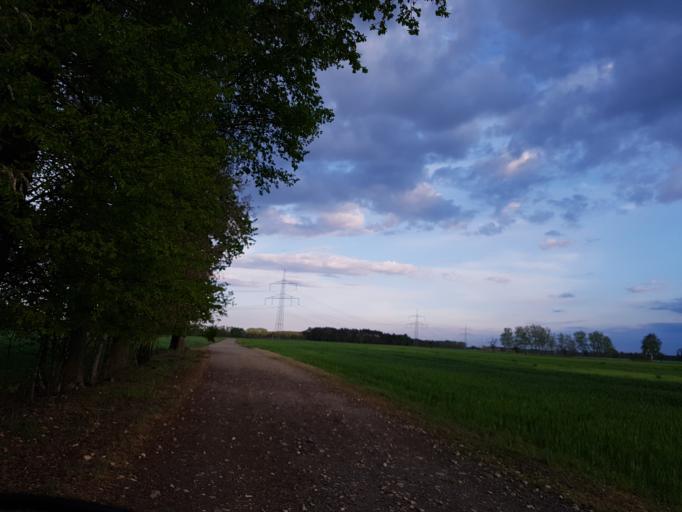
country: DE
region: Brandenburg
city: Schilda
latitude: 51.5682
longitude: 13.3860
